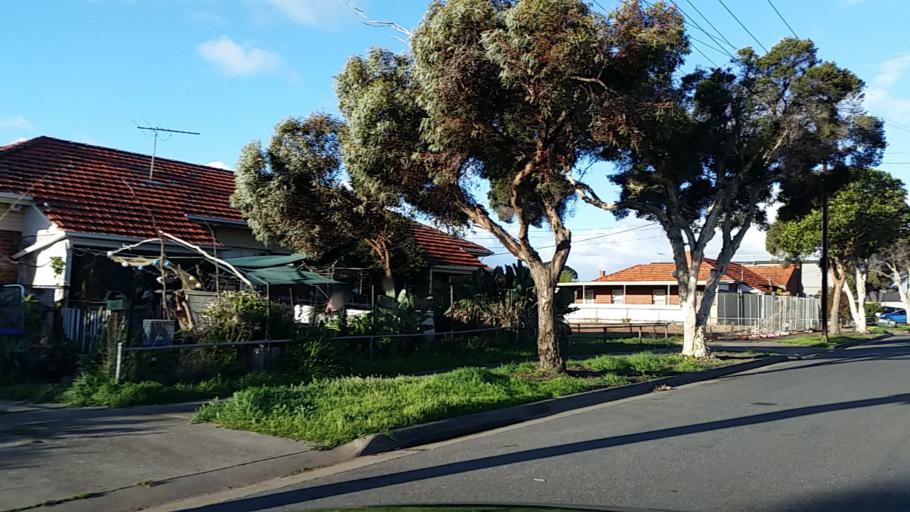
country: AU
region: South Australia
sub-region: Charles Sturt
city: Woodville West
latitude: -34.8862
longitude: 138.5226
